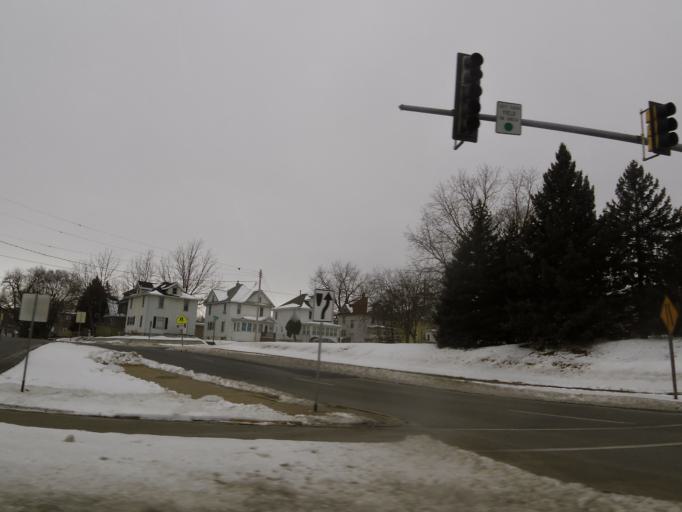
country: US
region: Iowa
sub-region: Black Hawk County
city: Waterloo
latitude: 42.4878
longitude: -92.3351
